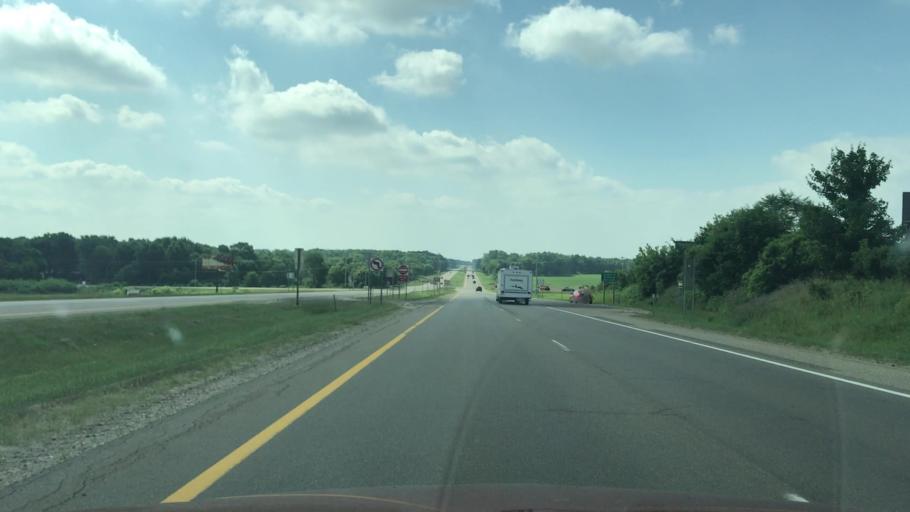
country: US
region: Michigan
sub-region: Kent County
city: Sparta
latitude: 43.1191
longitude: -85.7071
